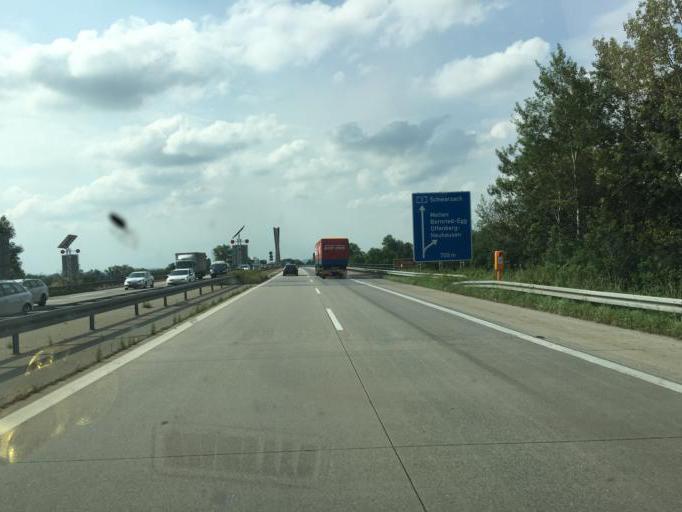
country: DE
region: Bavaria
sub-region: Lower Bavaria
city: Metten
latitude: 48.8405
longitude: 12.8982
